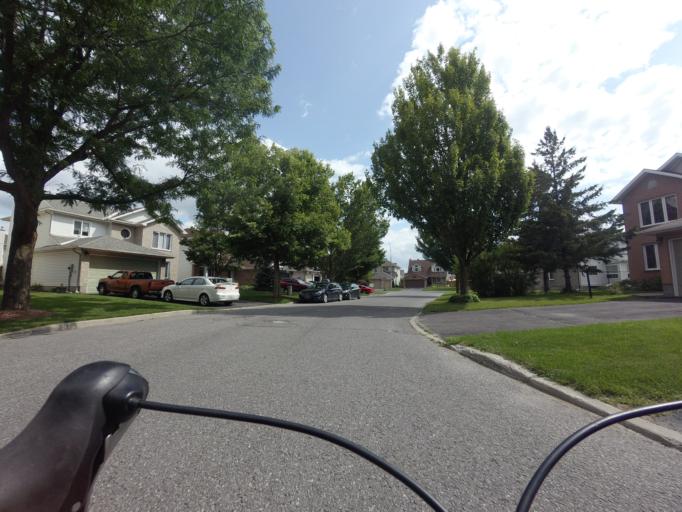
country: CA
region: Ontario
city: Bells Corners
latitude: 45.2755
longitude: -75.8533
